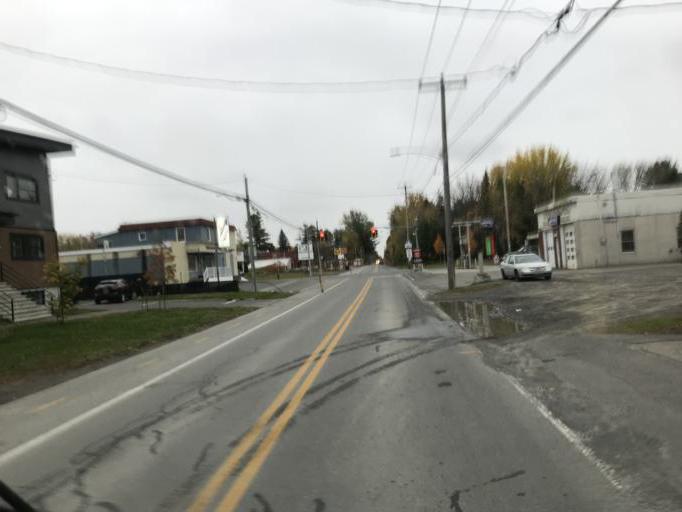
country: CA
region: Quebec
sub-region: Lanaudiere
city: Lorraine
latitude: 45.6845
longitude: -73.7897
